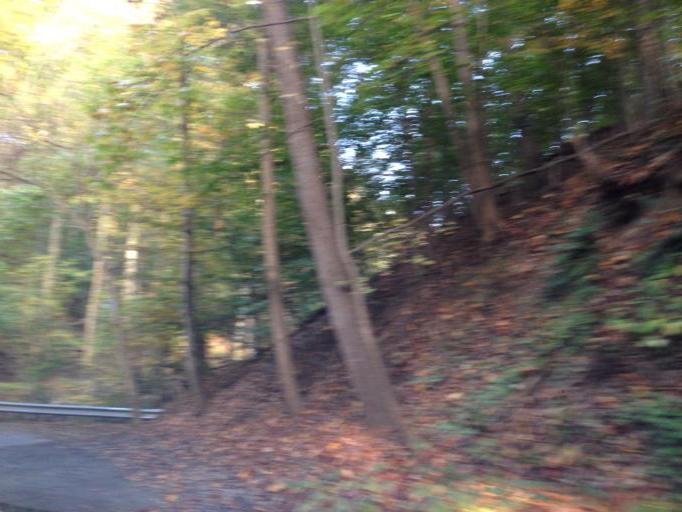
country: US
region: Maryland
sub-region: Howard County
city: Ellicott City
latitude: 39.2738
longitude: -76.7933
